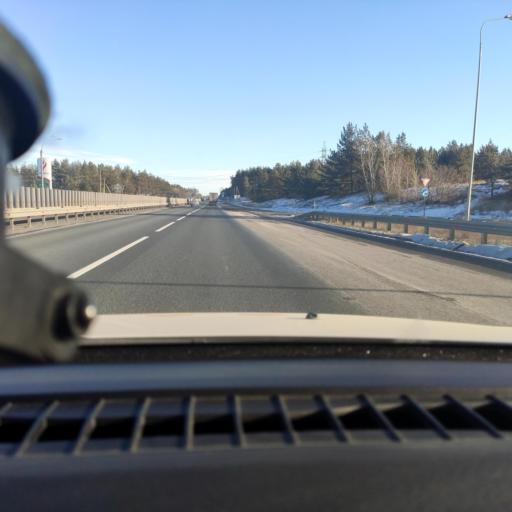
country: RU
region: Samara
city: Kurumoch
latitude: 53.4959
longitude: 50.0636
